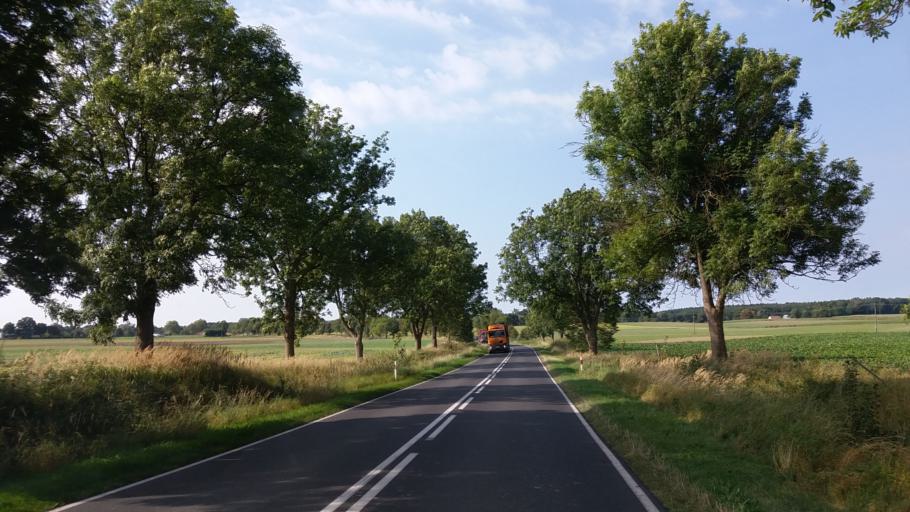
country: PL
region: West Pomeranian Voivodeship
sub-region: Powiat stargardzki
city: Suchan
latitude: 53.2380
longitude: 15.3074
